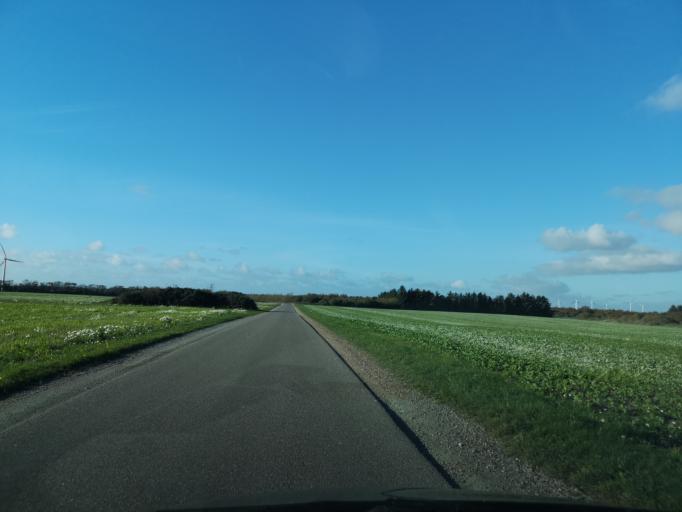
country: DK
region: Central Jutland
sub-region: Ringkobing-Skjern Kommune
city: Tarm
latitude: 55.8092
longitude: 8.4410
